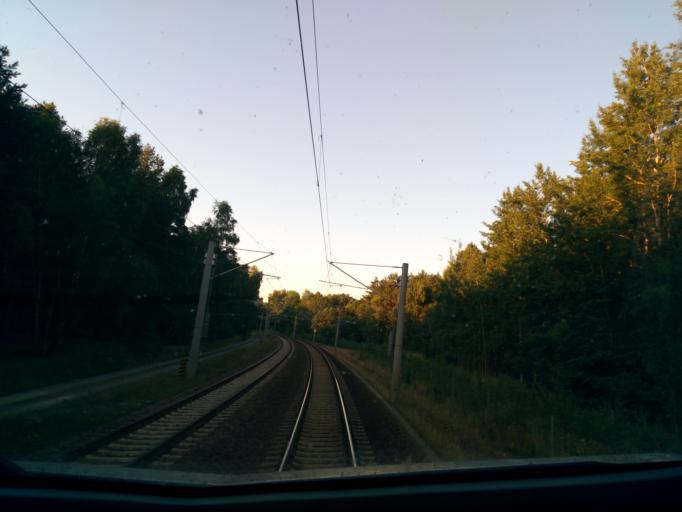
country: DE
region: Brandenburg
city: Bestensee
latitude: 52.2133
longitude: 13.6176
